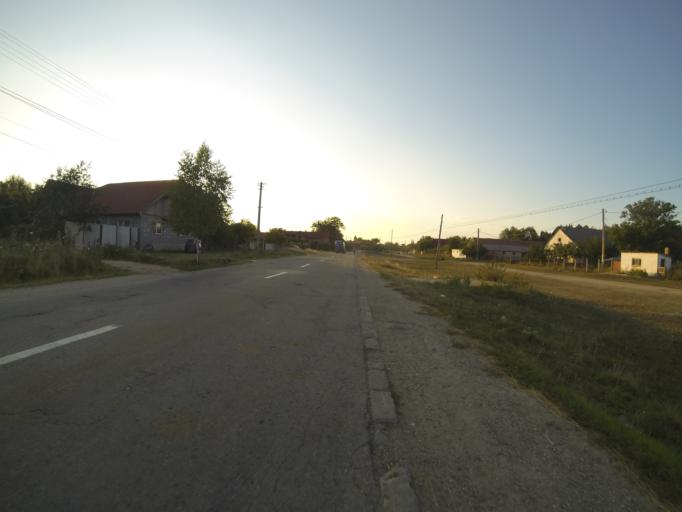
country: RO
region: Brasov
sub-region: Comuna Sinca Veche
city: Sinca Veche
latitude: 45.7591
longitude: 25.1721
